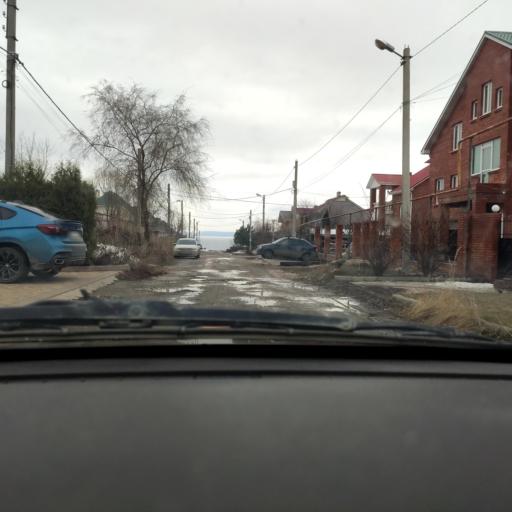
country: RU
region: Samara
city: Podstepki
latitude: 53.5123
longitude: 49.2103
